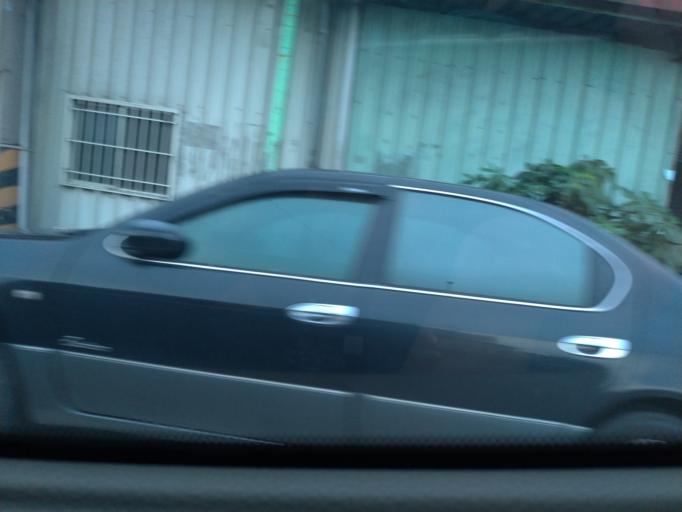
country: TW
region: Taiwan
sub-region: Taoyuan
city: Taoyuan
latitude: 24.9330
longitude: 121.3865
